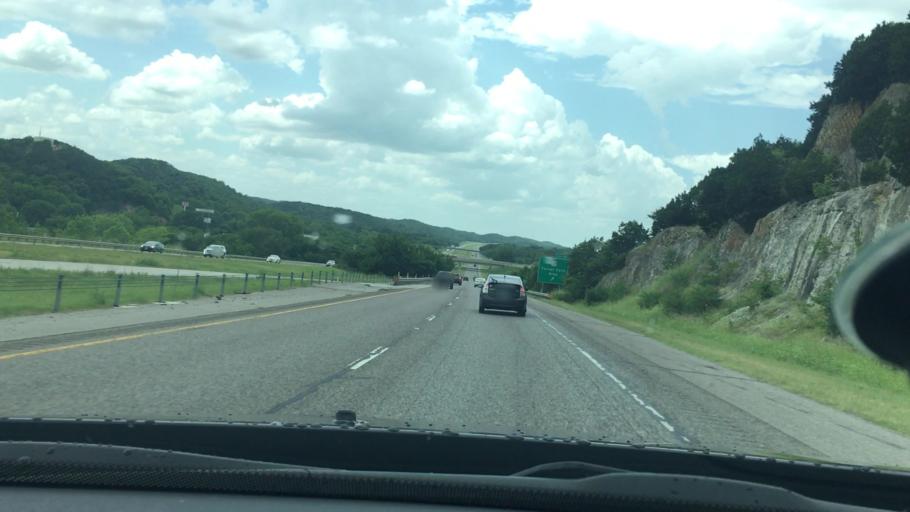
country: US
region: Oklahoma
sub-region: Murray County
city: Davis
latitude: 34.4457
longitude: -97.1303
